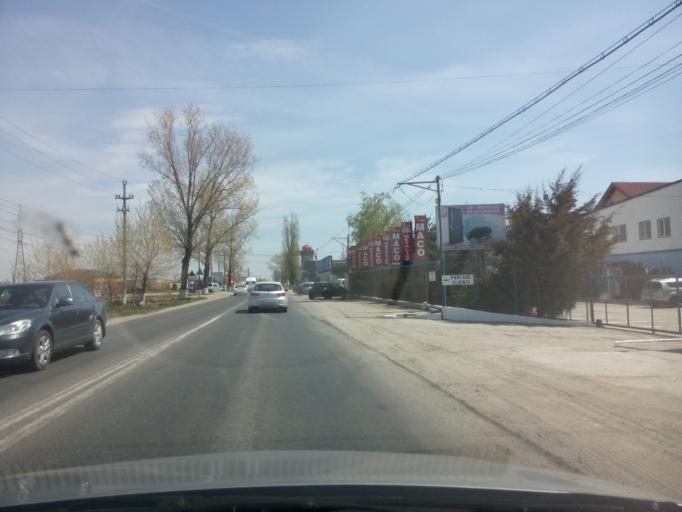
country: RO
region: Ilfov
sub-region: Comuna Pantelimon
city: Pantelimon
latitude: 44.4499
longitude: 26.2234
